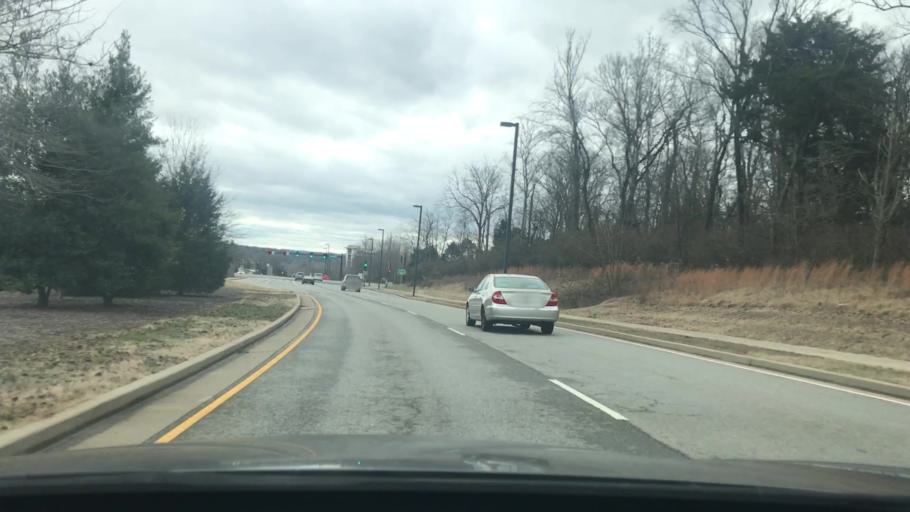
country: US
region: Tennessee
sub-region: Williamson County
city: Franklin
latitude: 35.9248
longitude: -86.8170
